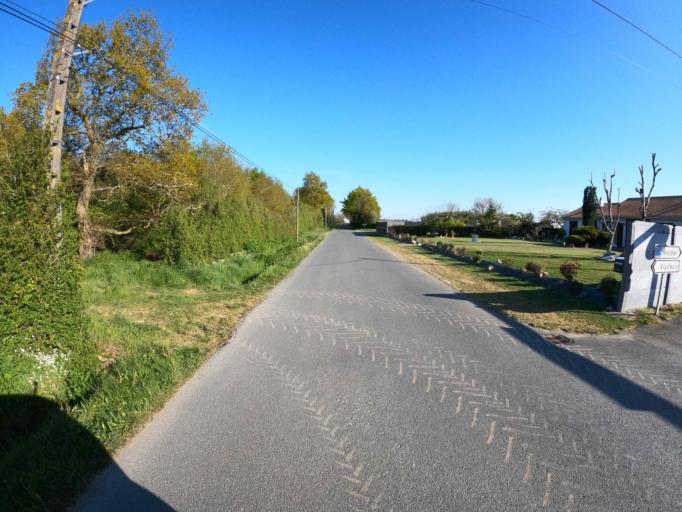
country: FR
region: Pays de la Loire
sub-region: Departement de la Vendee
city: Saint-Andre-Treize-Voies
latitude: 46.9008
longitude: -1.3737
